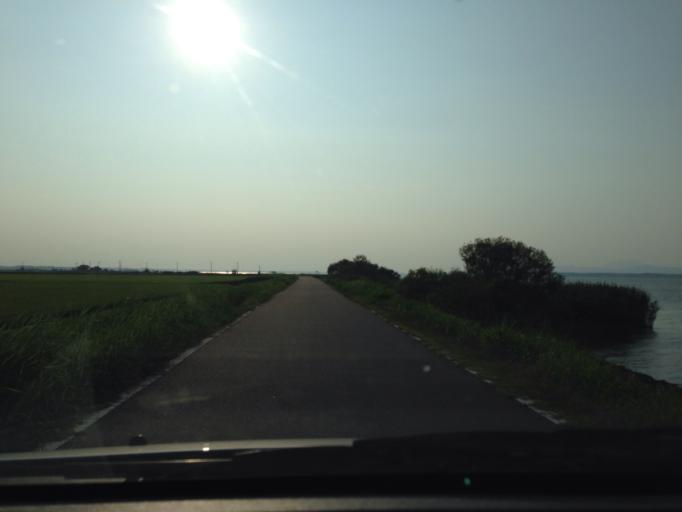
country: JP
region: Ibaraki
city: Inashiki
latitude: 36.0291
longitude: 140.3497
